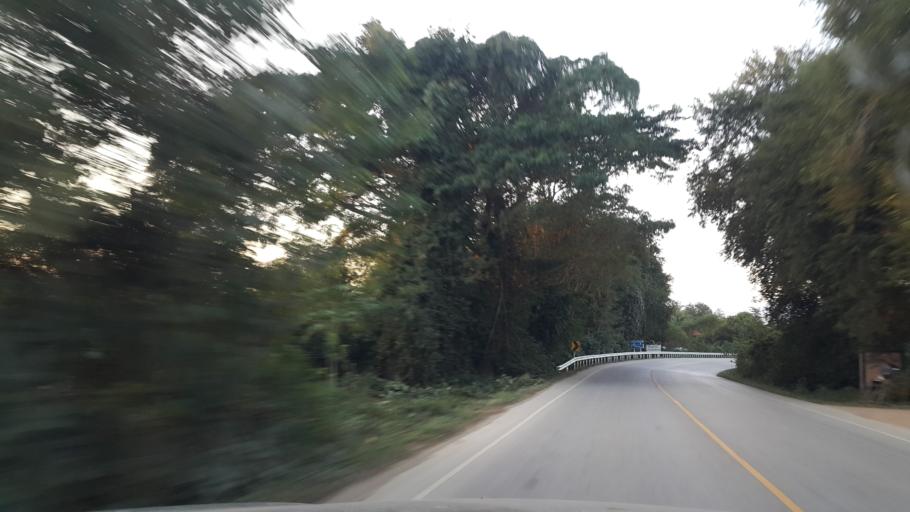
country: TH
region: Phrae
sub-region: Amphoe Wang Chin
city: Wang Chin
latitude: 17.8700
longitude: 99.6201
